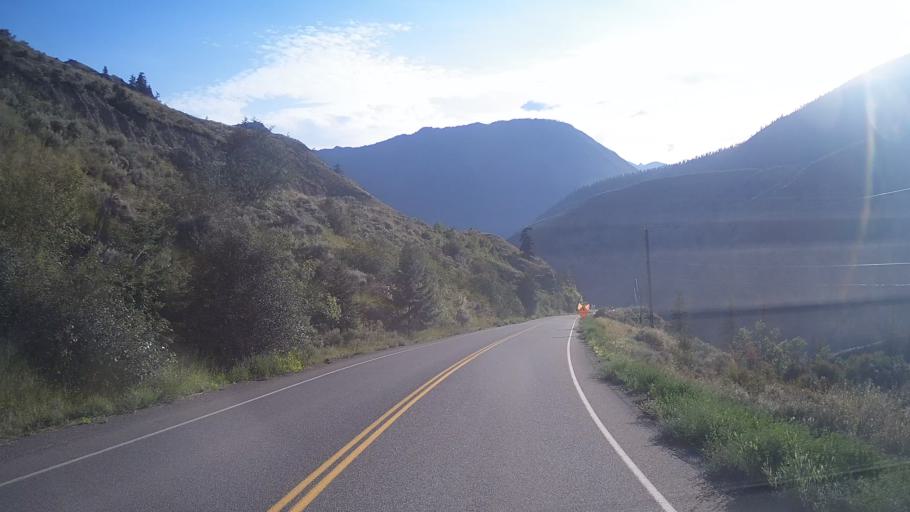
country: CA
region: British Columbia
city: Lillooet
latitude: 50.7553
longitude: -121.8329
